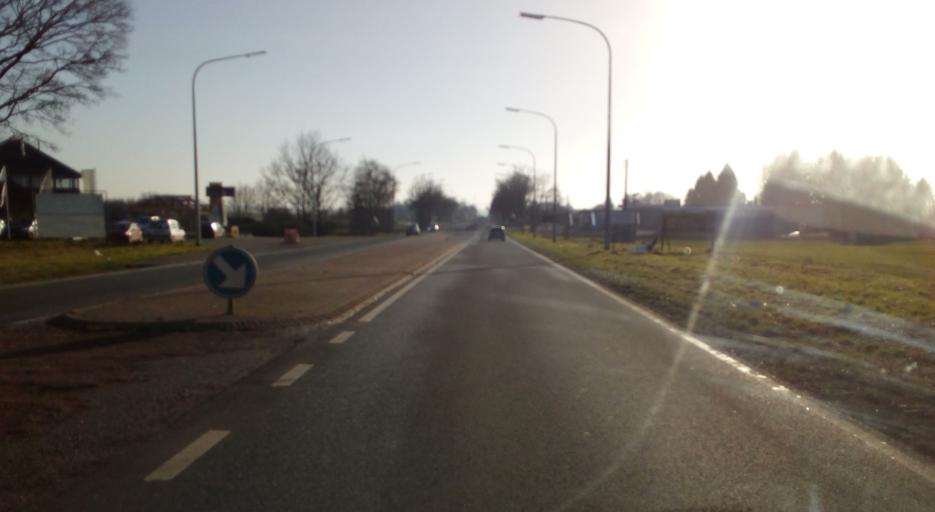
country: BE
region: Wallonia
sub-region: Province du Hainaut
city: Gerpinnes
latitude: 50.3142
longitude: 4.4790
